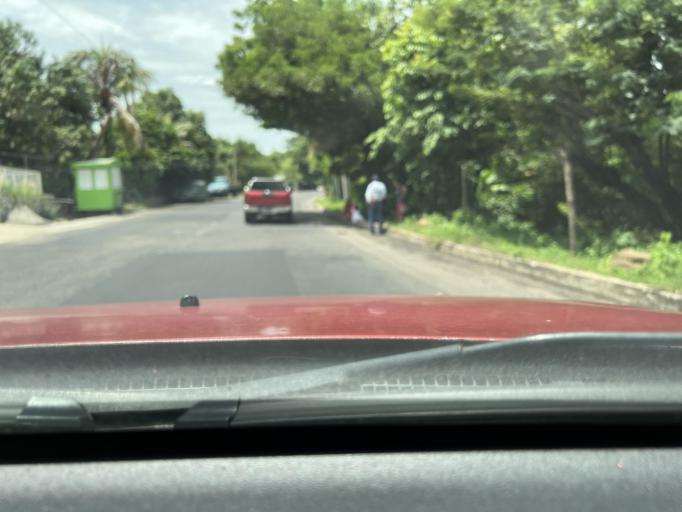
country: SV
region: Usulutan
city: Berlin
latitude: 13.6035
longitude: -88.5834
